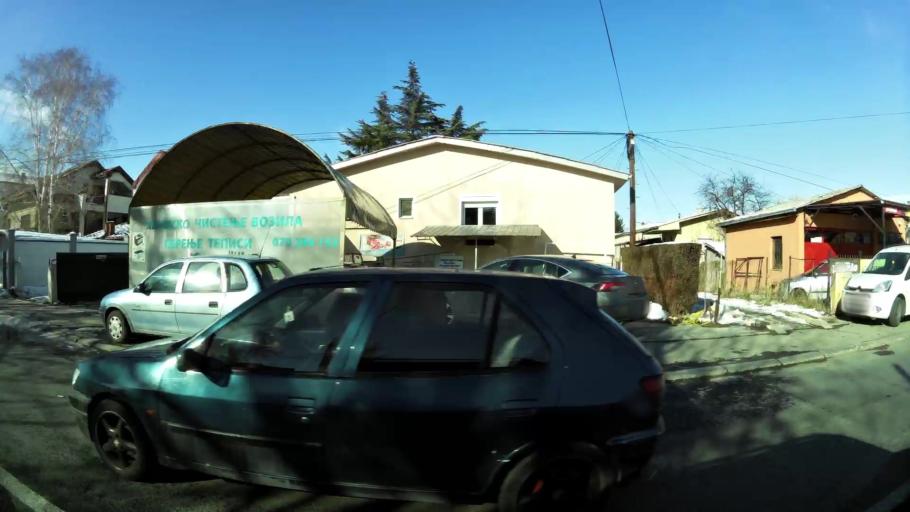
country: MK
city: Krushopek
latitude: 42.0105
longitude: 21.3741
